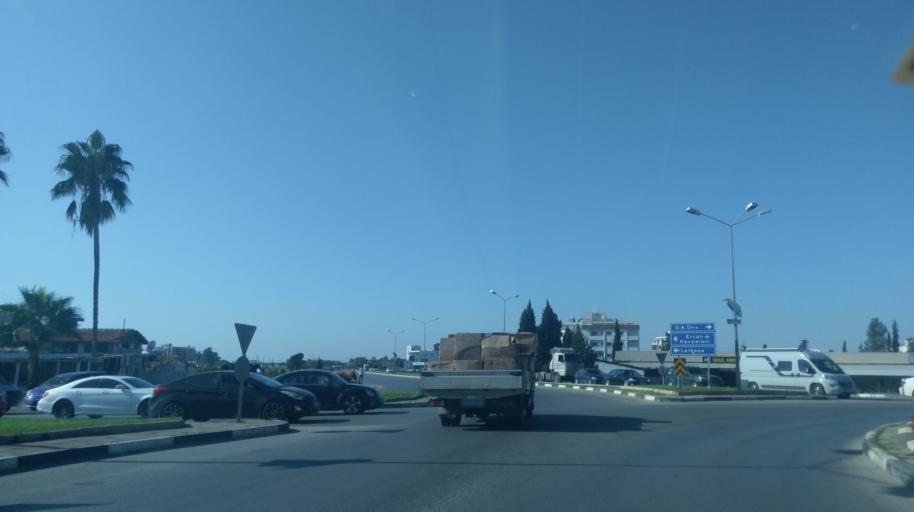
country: CY
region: Ammochostos
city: Famagusta
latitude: 35.1280
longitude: 33.9218
